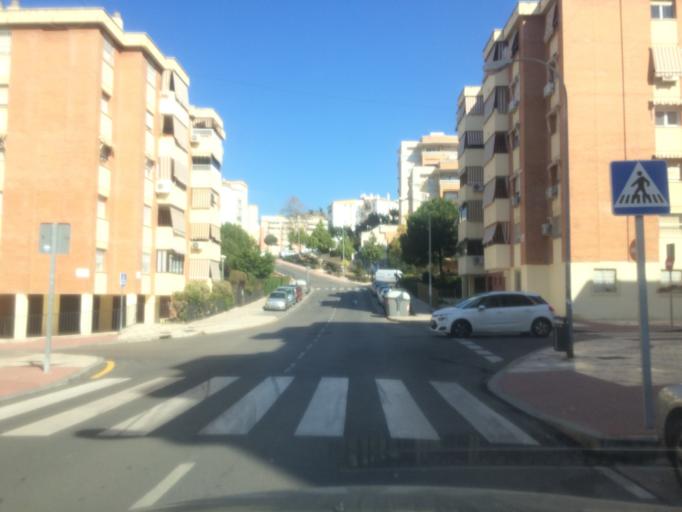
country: ES
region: Andalusia
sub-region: Provincia de Malaga
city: Malaga
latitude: 36.7476
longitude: -4.4173
